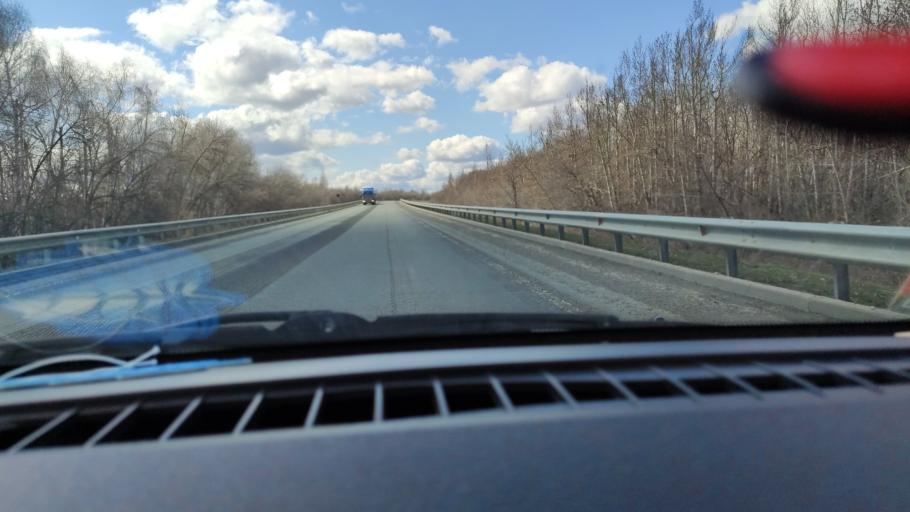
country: RU
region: Saratov
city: Dukhovnitskoye
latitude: 52.6236
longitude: 48.1767
